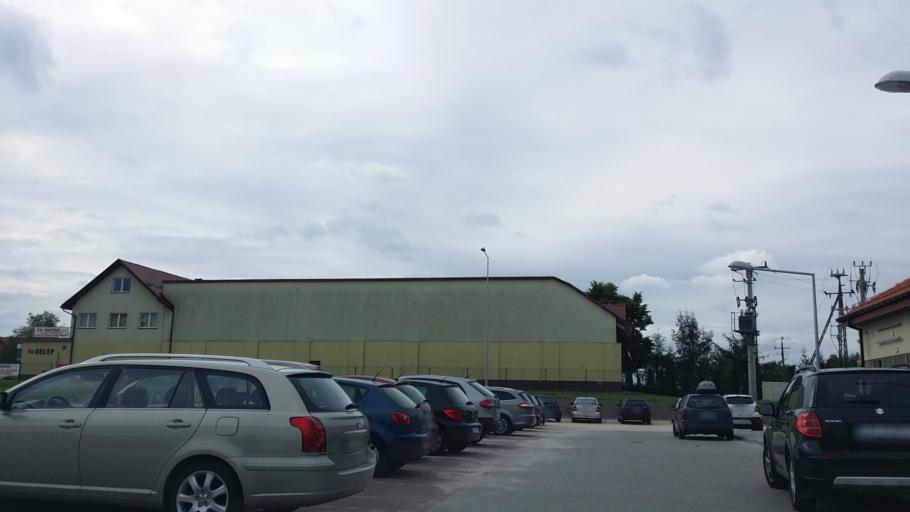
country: PL
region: Lesser Poland Voivodeship
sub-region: Powiat oswiecimski
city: Zator
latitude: 49.9967
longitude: 19.4317
